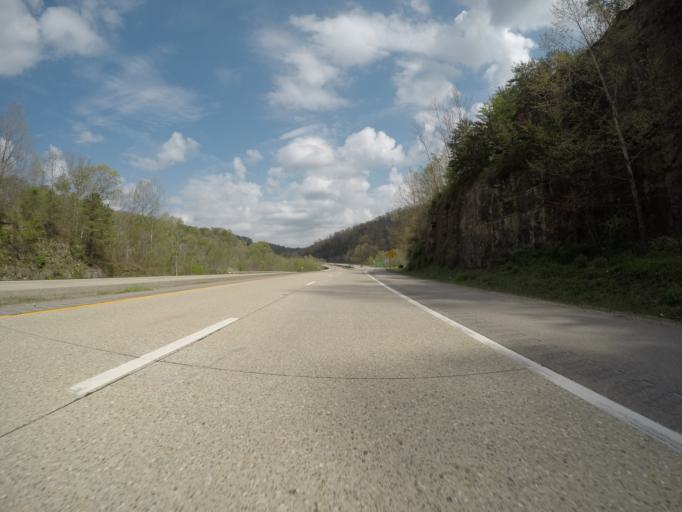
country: US
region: West Virginia
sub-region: Kanawha County
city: Alum Creek
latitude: 38.2195
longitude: -81.8342
